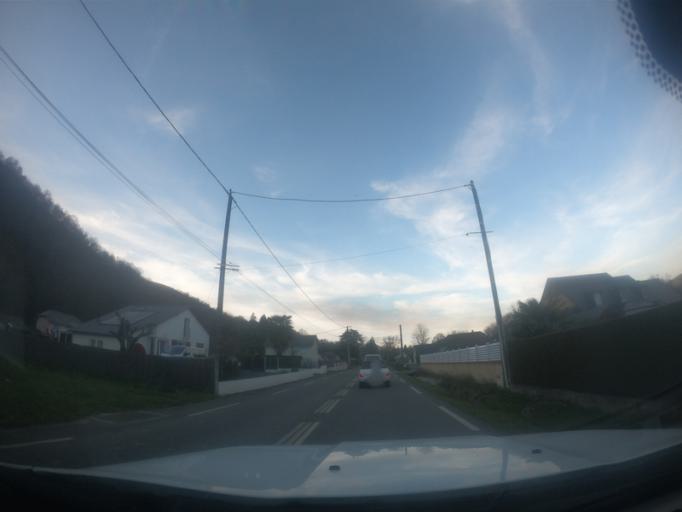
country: FR
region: Midi-Pyrenees
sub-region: Departement des Hautes-Pyrenees
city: Gerde
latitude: 43.0394
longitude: 0.1617
